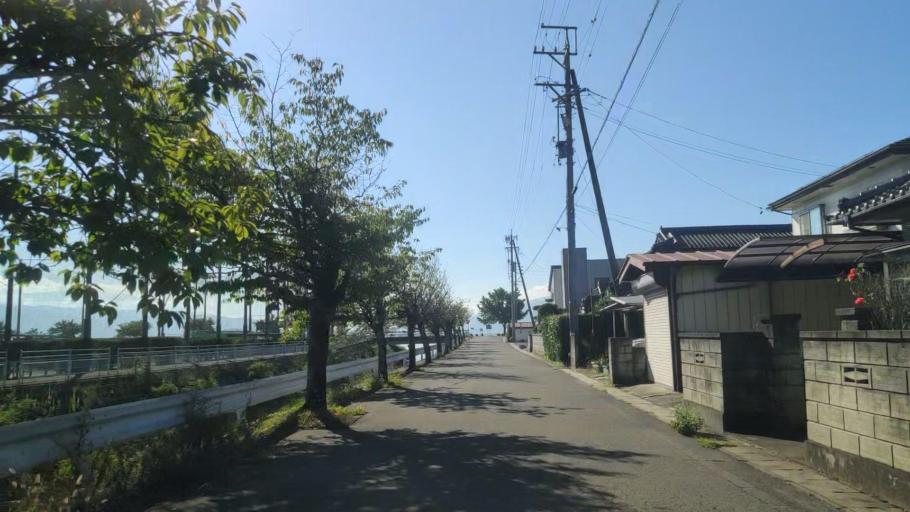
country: JP
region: Nagano
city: Okaya
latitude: 36.0566
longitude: 138.0585
